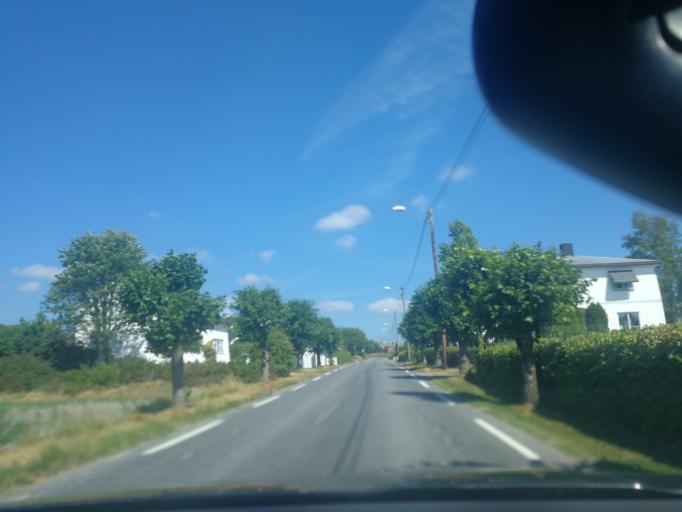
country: NO
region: Vestfold
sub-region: Stokke
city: Stokke
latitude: 59.2187
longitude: 10.2980
